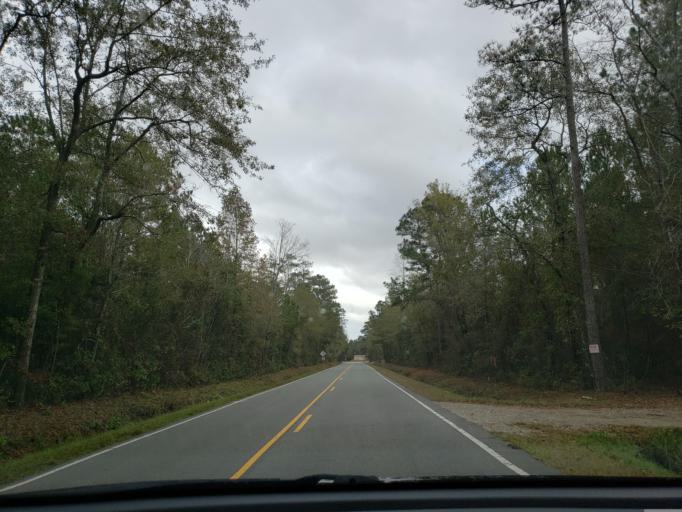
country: US
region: North Carolina
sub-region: Onslow County
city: Half Moon
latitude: 34.7209
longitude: -77.6217
